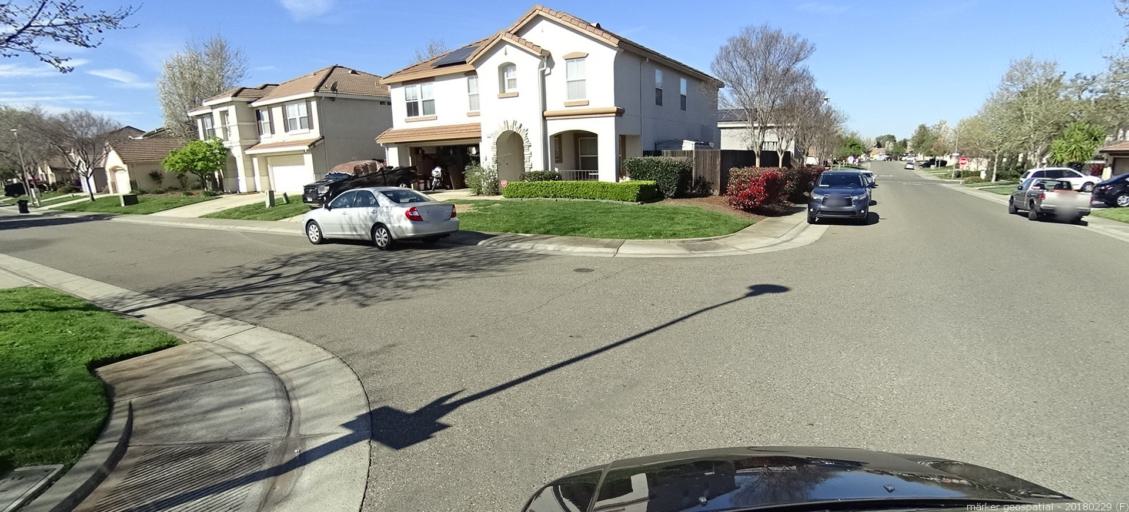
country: US
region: California
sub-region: Sacramento County
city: Rancho Cordova
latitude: 38.5487
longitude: -121.2801
